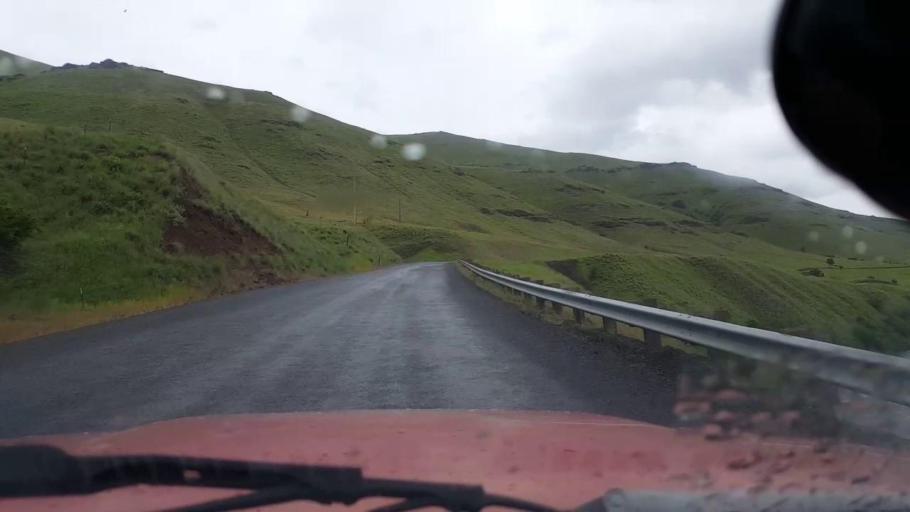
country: US
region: Washington
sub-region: Asotin County
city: Asotin
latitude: 46.0402
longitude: -117.2941
